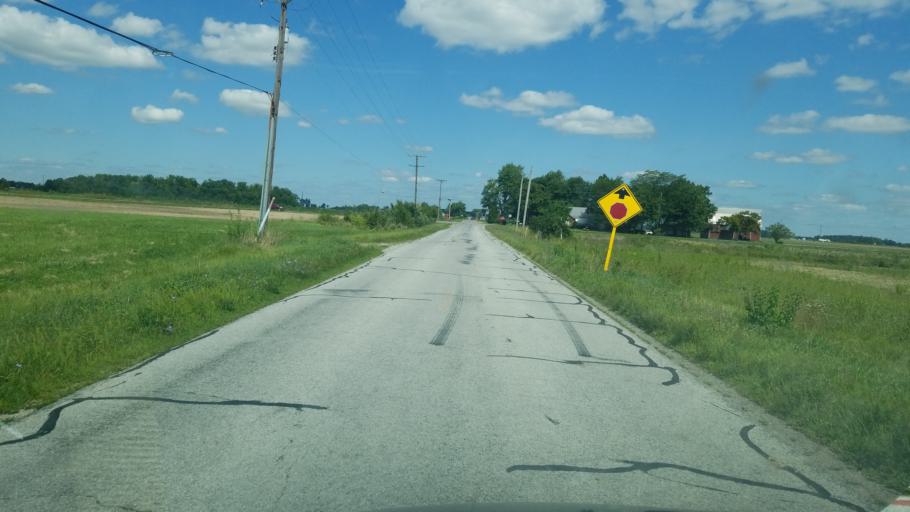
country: US
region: Ohio
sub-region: Fulton County
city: Swanton
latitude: 41.5866
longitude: -83.9407
